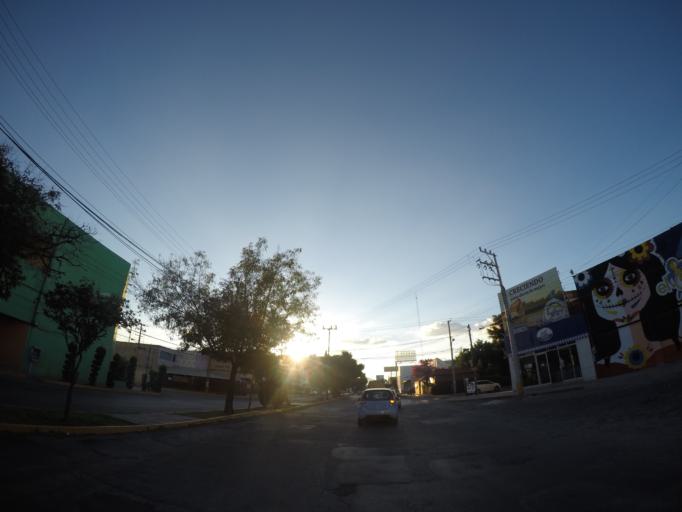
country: MX
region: San Luis Potosi
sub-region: San Luis Potosi
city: San Luis Potosi
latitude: 22.1431
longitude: -101.0005
